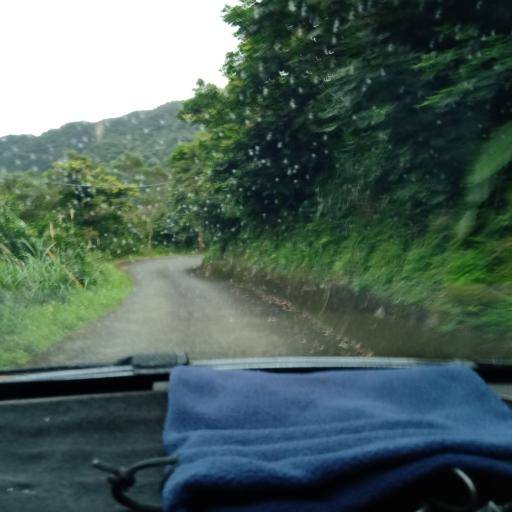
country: TW
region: Taiwan
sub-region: Yilan
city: Yilan
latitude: 24.8098
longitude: 121.6973
